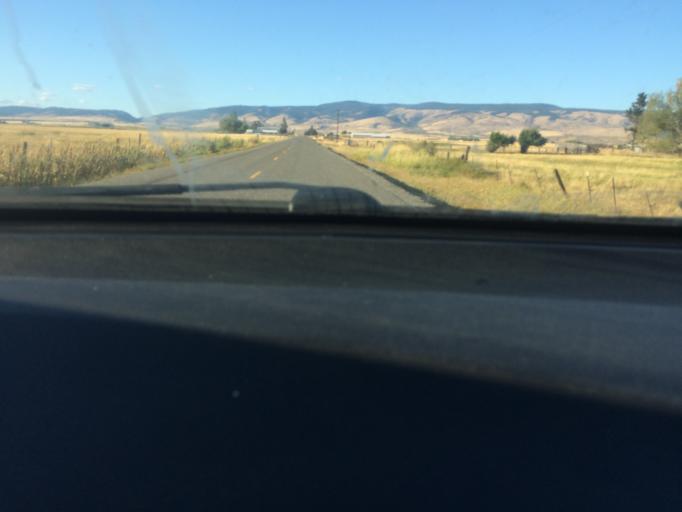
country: US
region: Washington
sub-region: Kittitas County
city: Ellensburg
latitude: 47.0833
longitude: -120.6037
